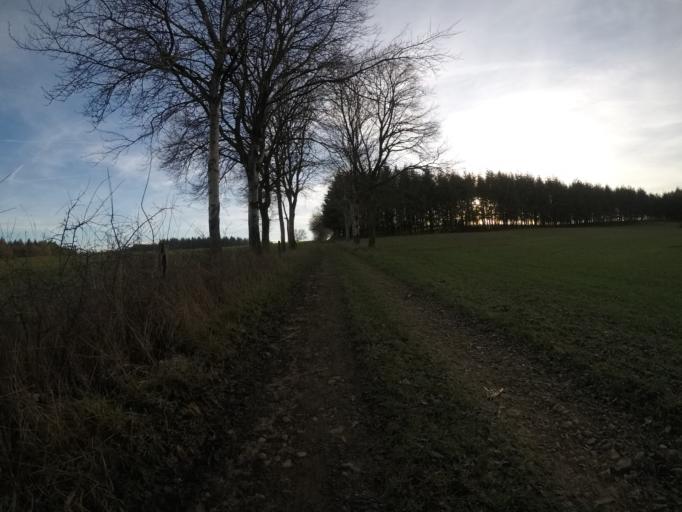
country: BE
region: Wallonia
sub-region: Province du Luxembourg
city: Tintigny
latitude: 49.6849
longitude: 5.4868
